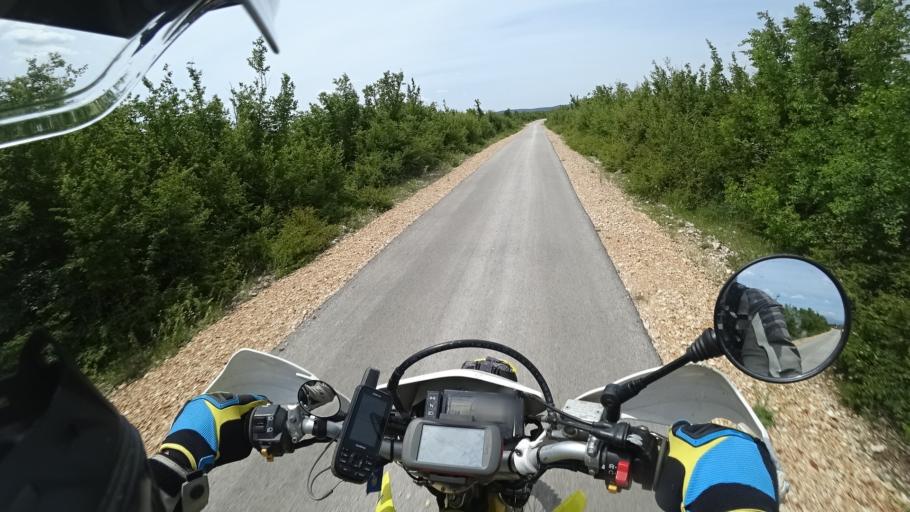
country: HR
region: Sibensko-Kniniska
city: Kistanje
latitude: 44.0725
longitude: 15.9880
